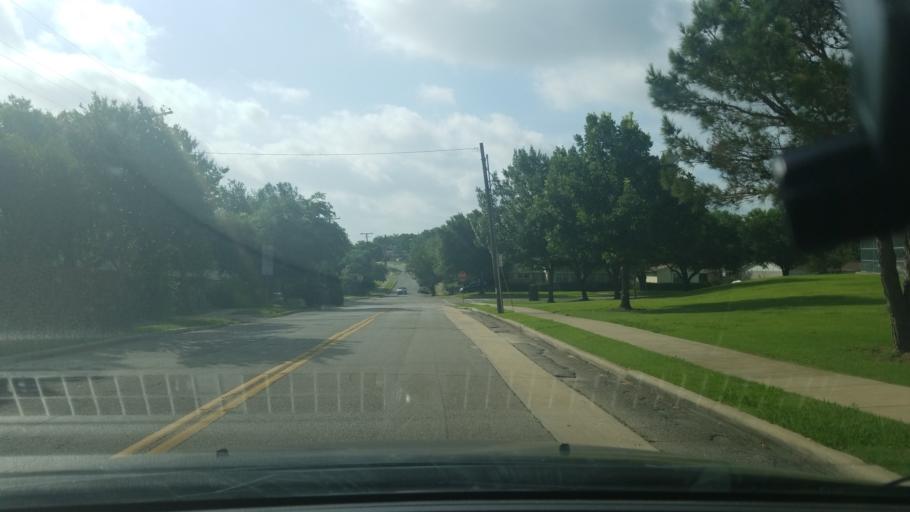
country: US
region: Texas
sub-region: Dallas County
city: Mesquite
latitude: 32.7712
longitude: -96.6328
